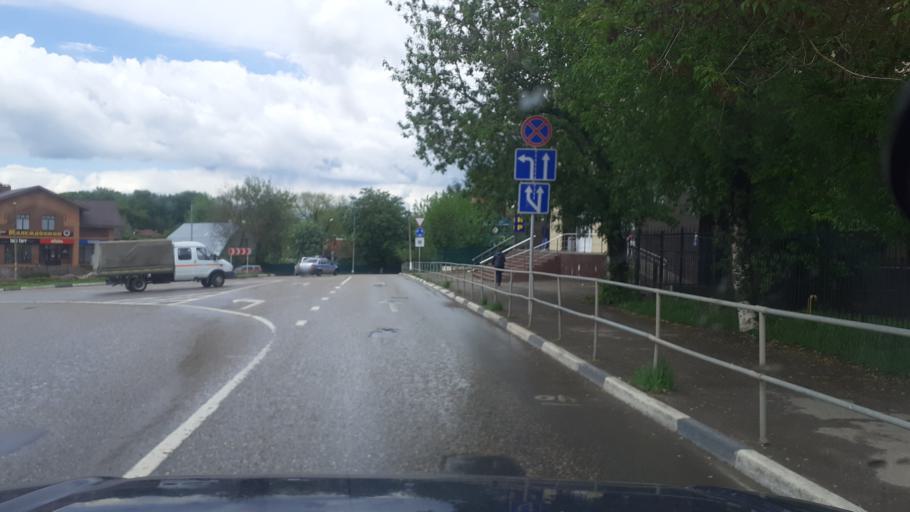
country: RU
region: Moskovskaya
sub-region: Volokolamskiy Rayon
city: Volokolamsk
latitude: 56.0314
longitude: 35.9590
